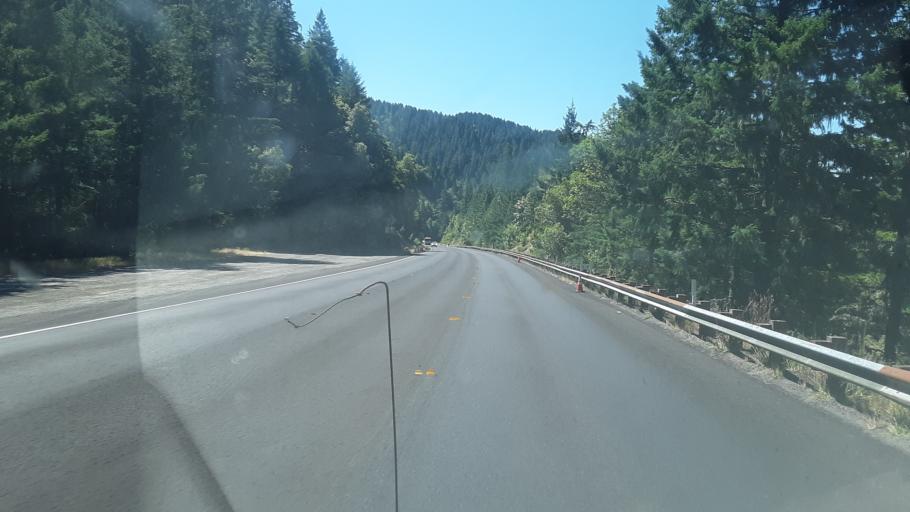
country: US
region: Oregon
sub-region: Josephine County
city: Cave Junction
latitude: 41.9601
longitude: -123.7458
